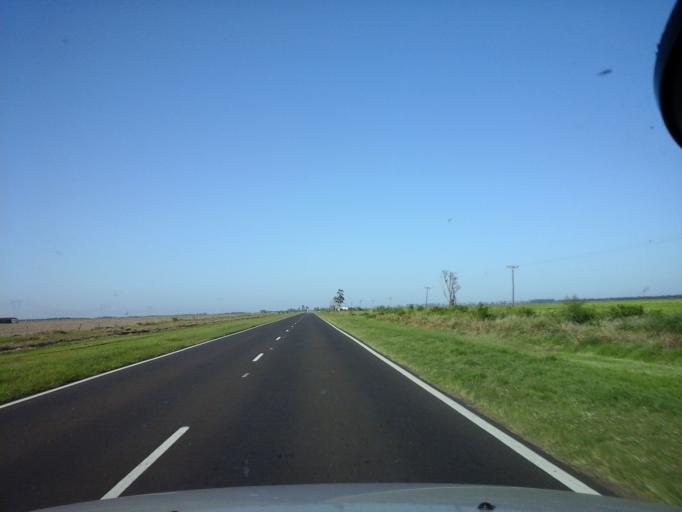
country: AR
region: Corrientes
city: Ita Ibate
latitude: -27.4507
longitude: -57.4097
